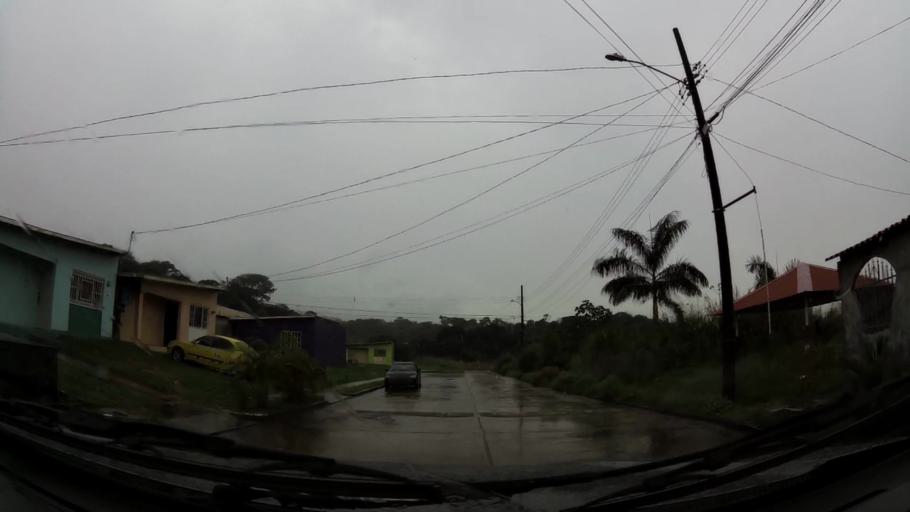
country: PA
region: Colon
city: Puerto Pilon
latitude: 9.3543
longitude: -79.7953
